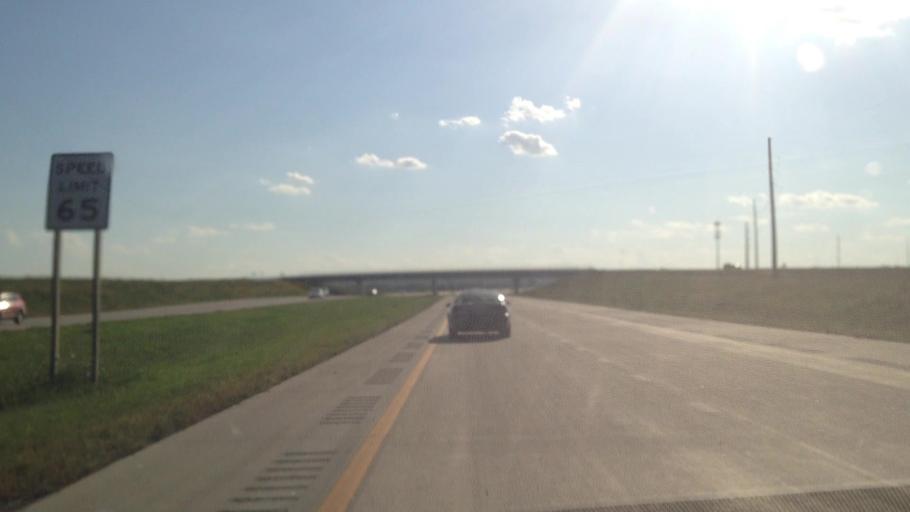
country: US
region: Kansas
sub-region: Douglas County
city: Lawrence
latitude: 38.9230
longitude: -95.2483
